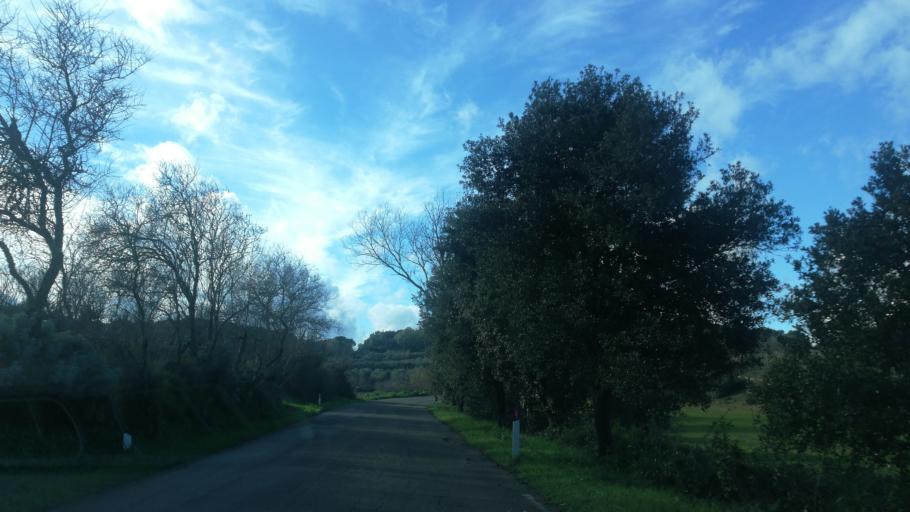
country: IT
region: Sardinia
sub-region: Provincia di Medio Campidano
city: Villanovaforru
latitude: 39.6335
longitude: 8.8612
